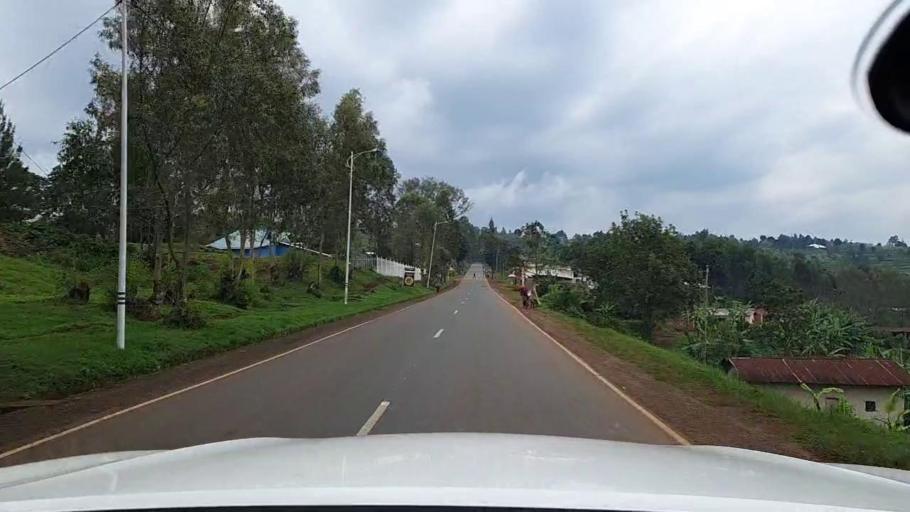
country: RW
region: Western Province
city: Cyangugu
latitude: -2.5374
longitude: 28.8947
